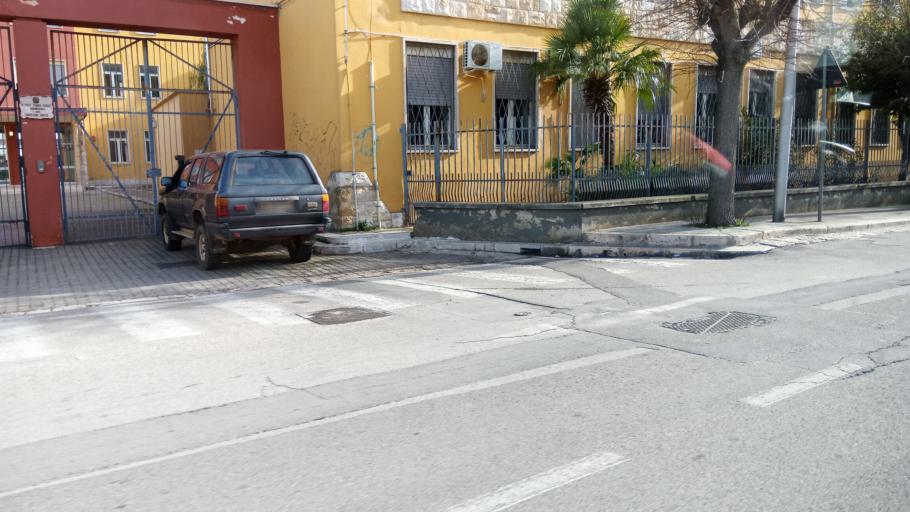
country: IT
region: Apulia
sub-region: Provincia di Bari
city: Castellana
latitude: 40.8884
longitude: 17.1674
